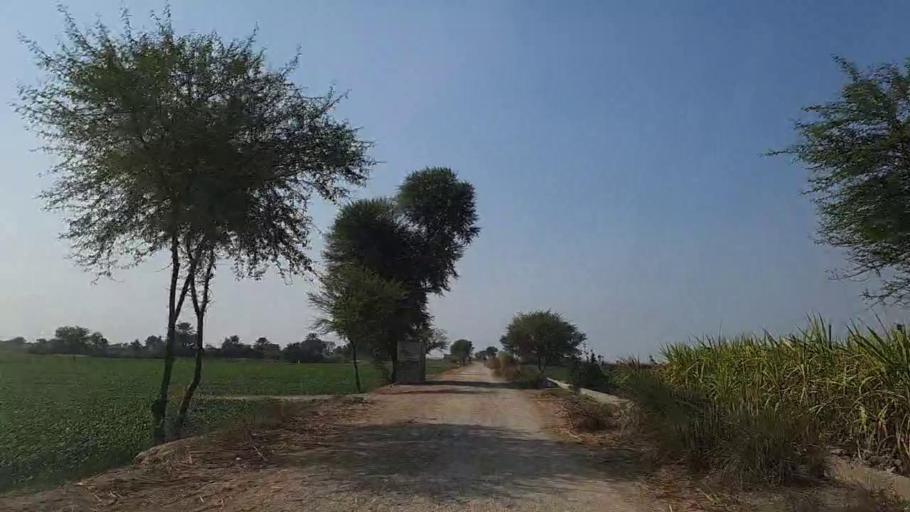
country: PK
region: Sindh
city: Daur
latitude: 26.4961
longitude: 68.2683
